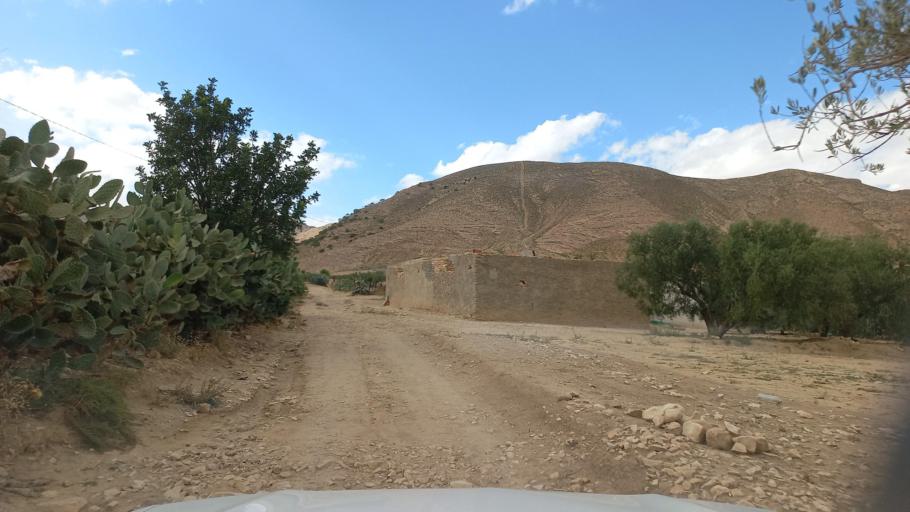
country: TN
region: Al Qasrayn
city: Sbiba
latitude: 35.4517
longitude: 9.0641
